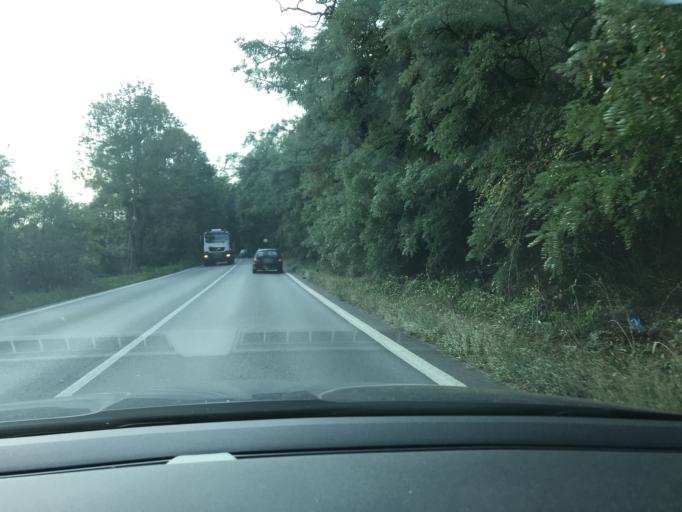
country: CZ
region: Central Bohemia
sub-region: Okres Kladno
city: Slany
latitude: 50.2355
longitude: 14.1000
